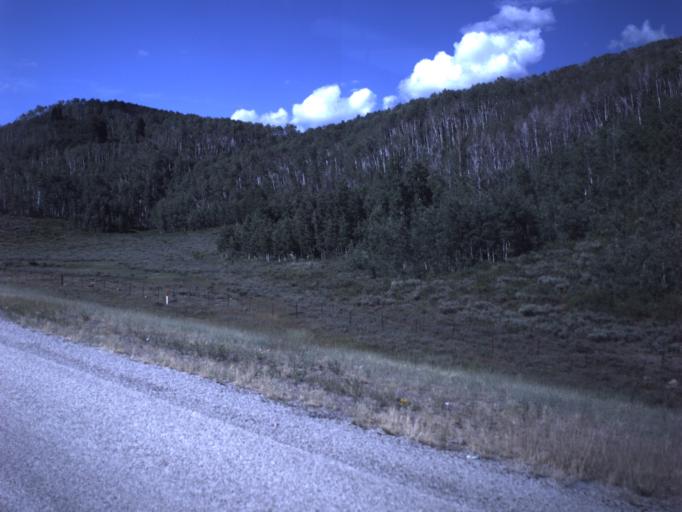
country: US
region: Utah
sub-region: Wasatch County
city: Heber
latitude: 40.2941
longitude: -111.2506
